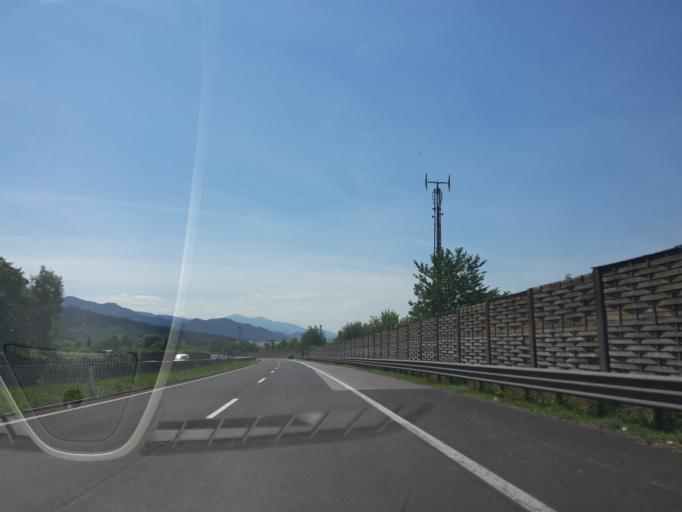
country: AT
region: Styria
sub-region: Politischer Bezirk Bruck-Muerzzuschlag
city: Kindberg
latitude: 47.5034
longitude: 15.4427
